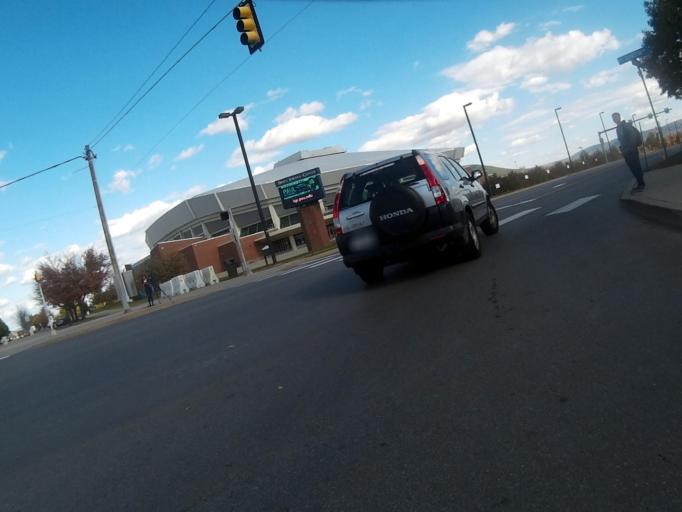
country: US
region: Pennsylvania
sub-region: Centre County
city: State College
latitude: 40.8081
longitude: -77.8576
